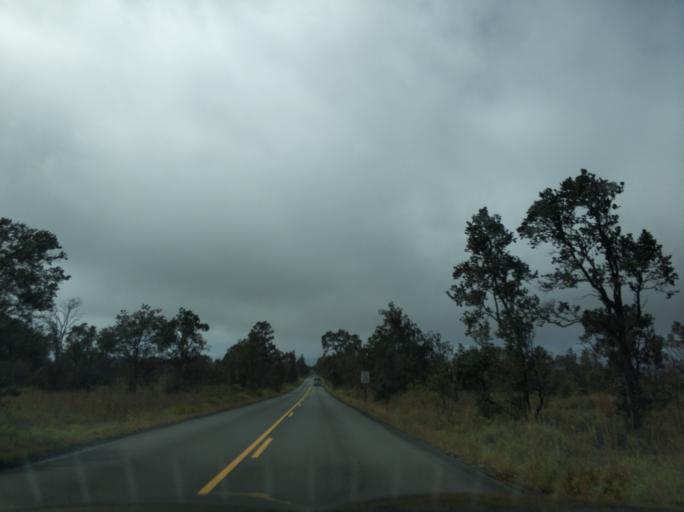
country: US
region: Hawaii
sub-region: Hawaii County
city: Volcano
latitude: 19.4288
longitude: -155.2832
